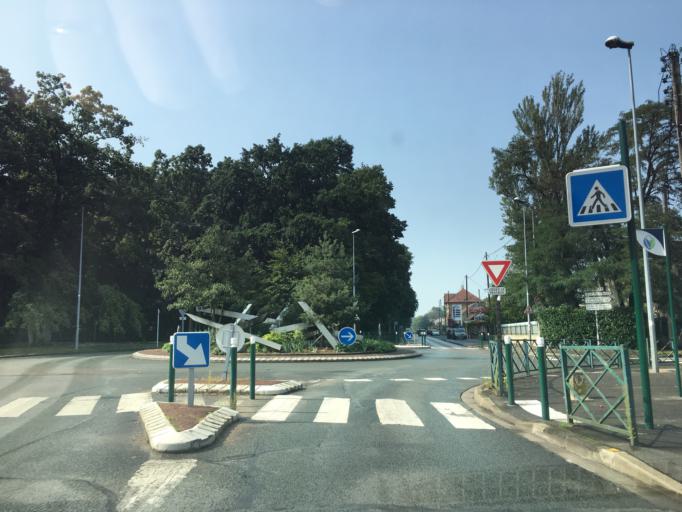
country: FR
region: Ile-de-France
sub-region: Departement du Val-de-Marne
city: Sucy-en-Brie
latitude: 48.7617
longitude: 2.5337
